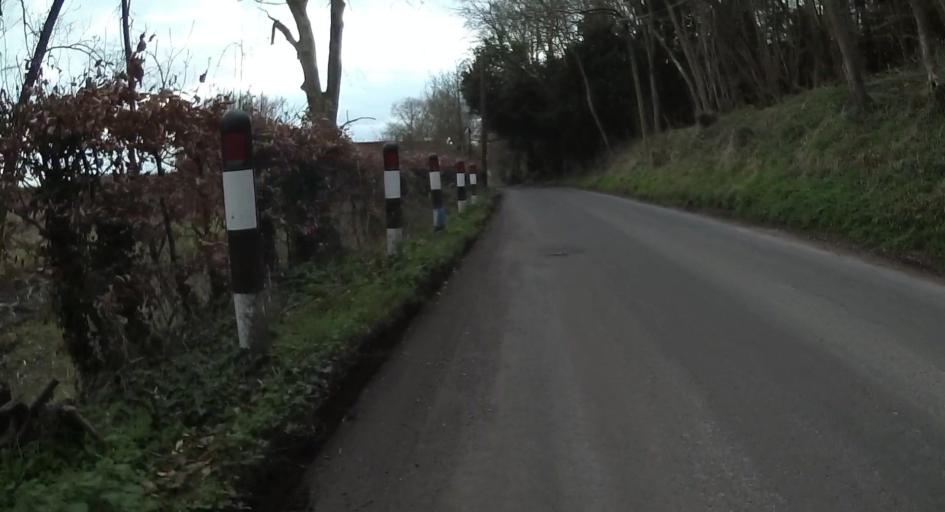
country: GB
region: England
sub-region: Hampshire
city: Andover
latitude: 51.1587
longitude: -1.4547
